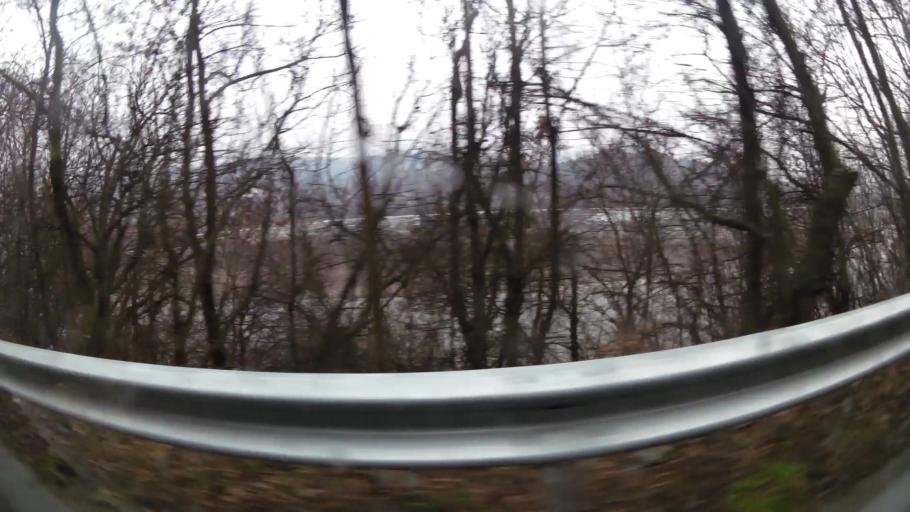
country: BG
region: Sofia-Capital
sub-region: Stolichna Obshtina
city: Sofia
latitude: 42.5913
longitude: 23.4240
